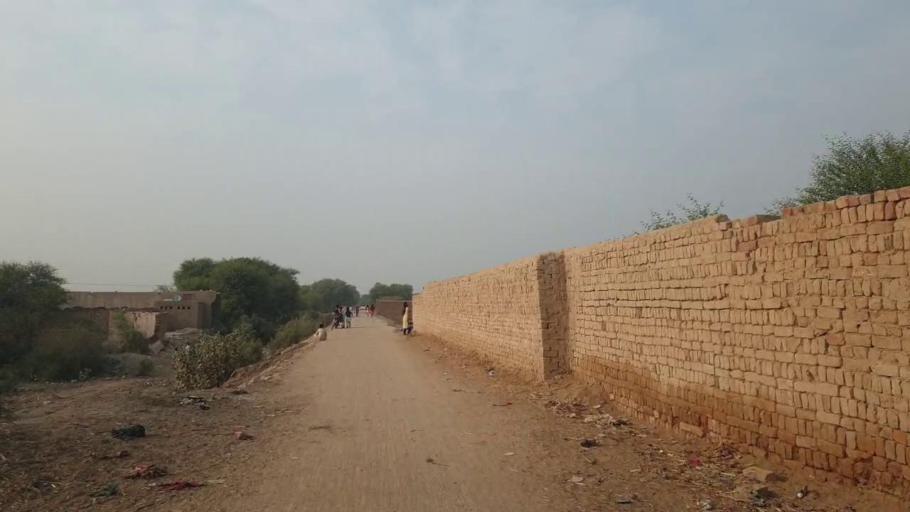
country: PK
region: Sindh
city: Sann
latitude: 26.1388
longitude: 68.0509
